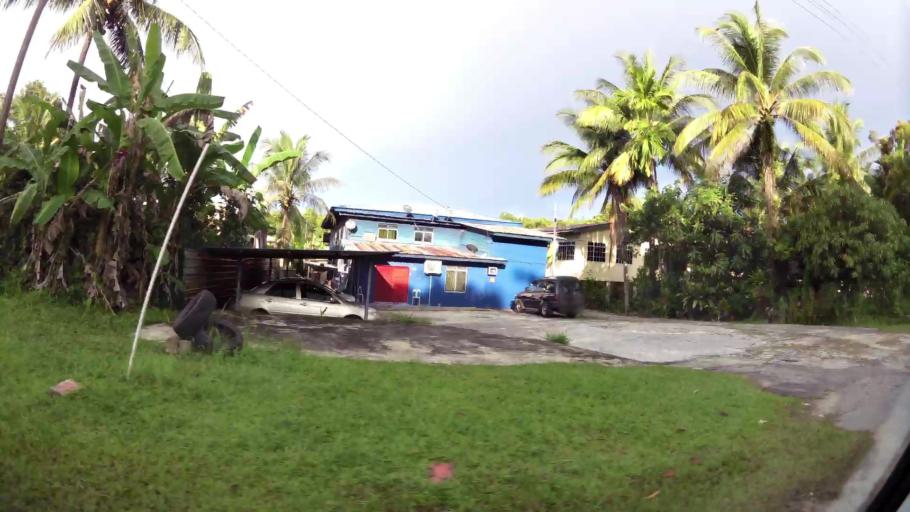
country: BN
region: Brunei and Muara
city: Bandar Seri Begawan
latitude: 4.9481
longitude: 115.0196
